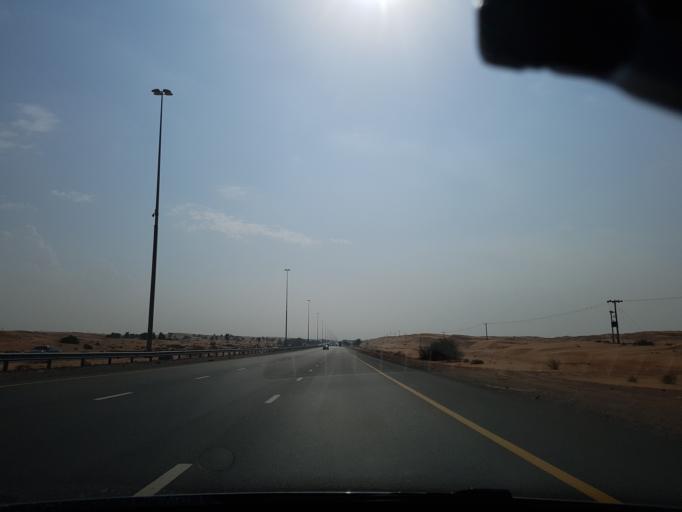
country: AE
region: Umm al Qaywayn
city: Umm al Qaywayn
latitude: 25.5157
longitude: 55.7087
